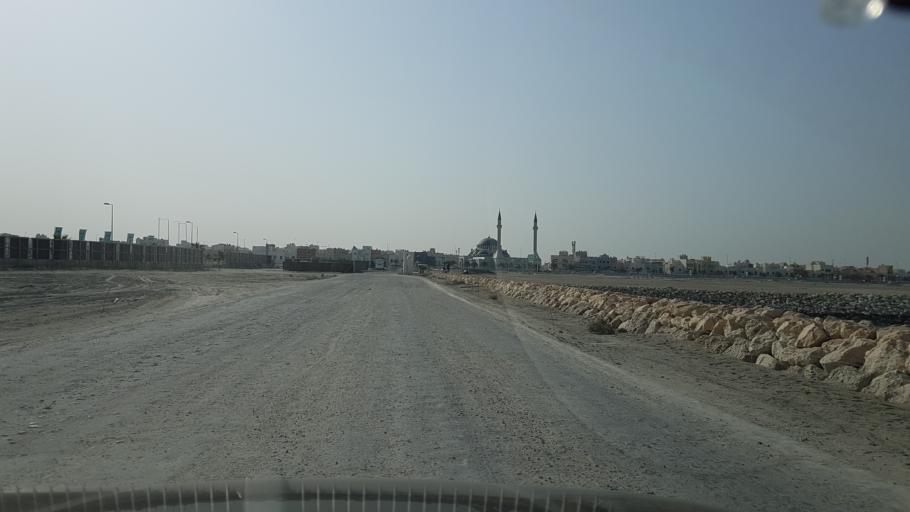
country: BH
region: Muharraq
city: Al Hadd
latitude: 26.2711
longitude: 50.6654
